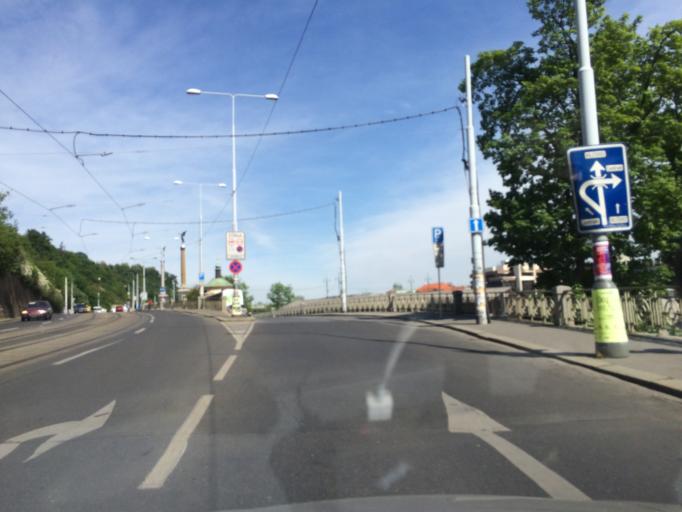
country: CZ
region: Praha
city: Prague
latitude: 50.0929
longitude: 14.4139
